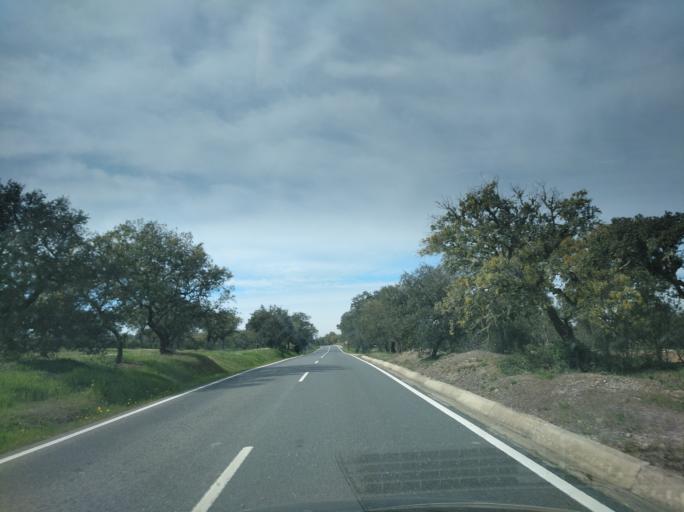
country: PT
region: Beja
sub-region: Mertola
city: Mertola
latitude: 37.7392
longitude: -7.7809
